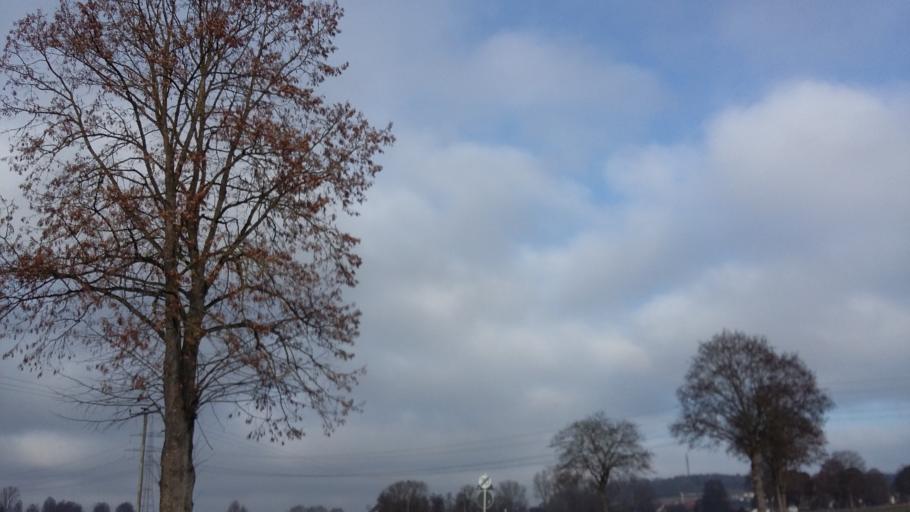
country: DE
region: Bavaria
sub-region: Swabia
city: Sielenbach
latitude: 48.4227
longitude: 11.1492
